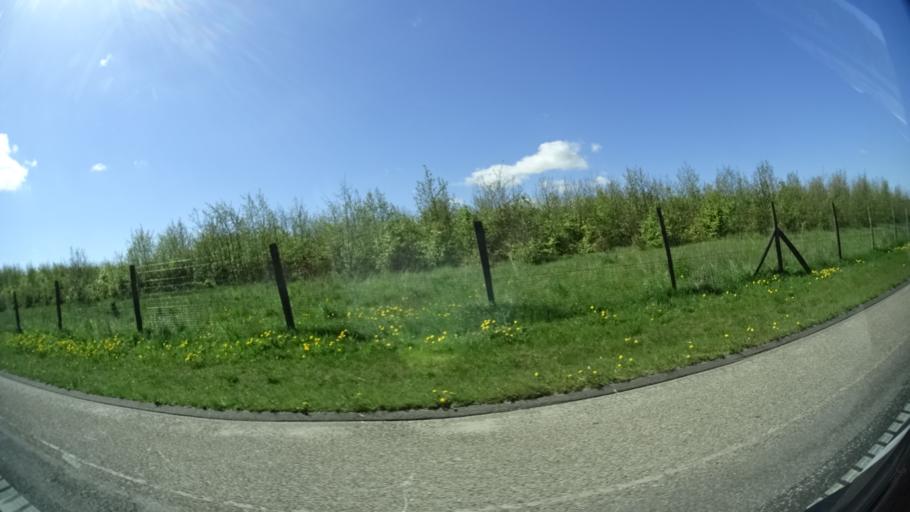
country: DK
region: Central Jutland
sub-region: Arhus Kommune
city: Sabro
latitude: 56.1835
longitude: 10.0695
